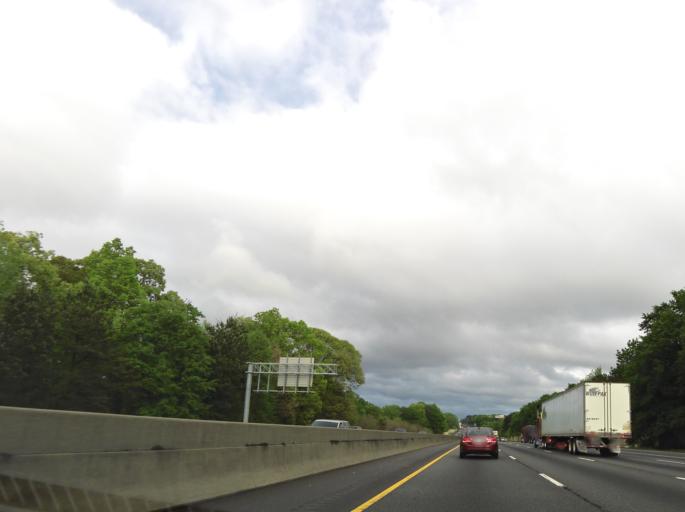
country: US
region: Georgia
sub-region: Clayton County
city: Morrow
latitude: 33.5843
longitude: -84.3750
